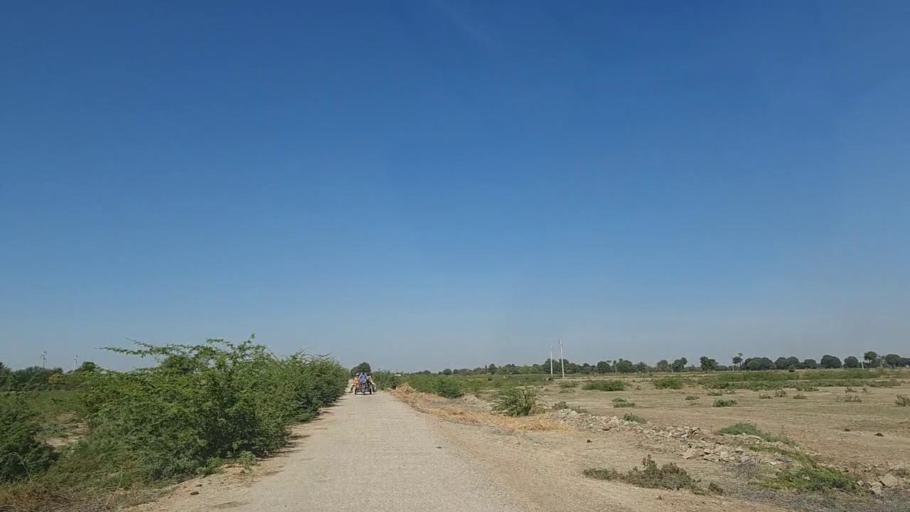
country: PK
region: Sindh
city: Samaro
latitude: 25.2986
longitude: 69.5147
